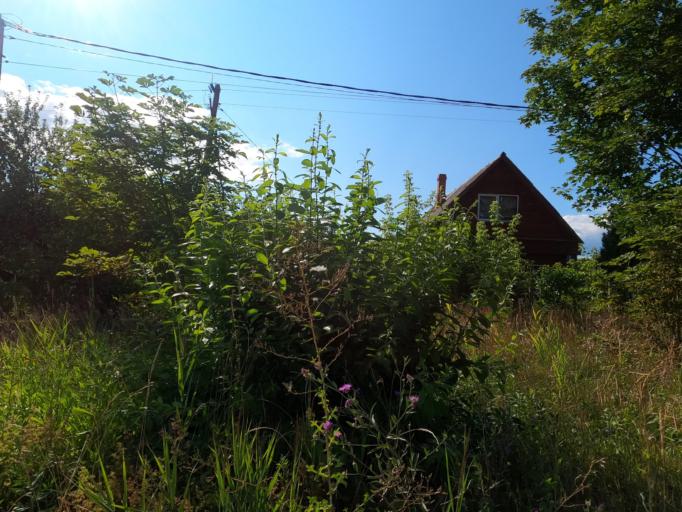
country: RU
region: Moskovskaya
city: Lopatinskiy
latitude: 55.3889
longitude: 38.7134
